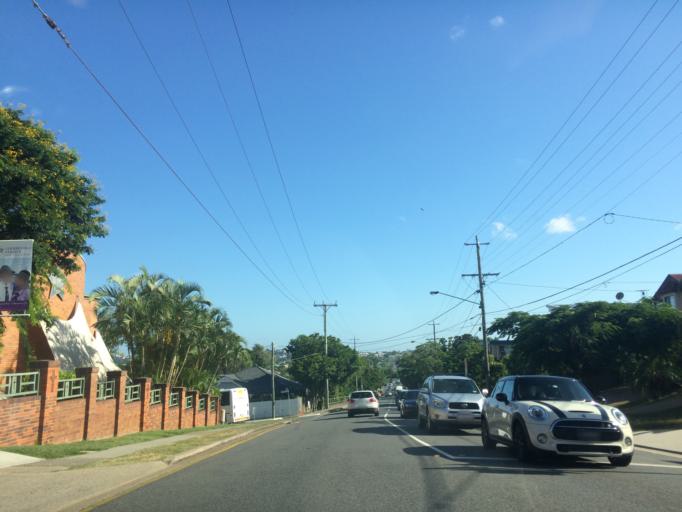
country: AU
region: Queensland
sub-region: Brisbane
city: Balmoral
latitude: -27.4693
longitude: 153.0591
